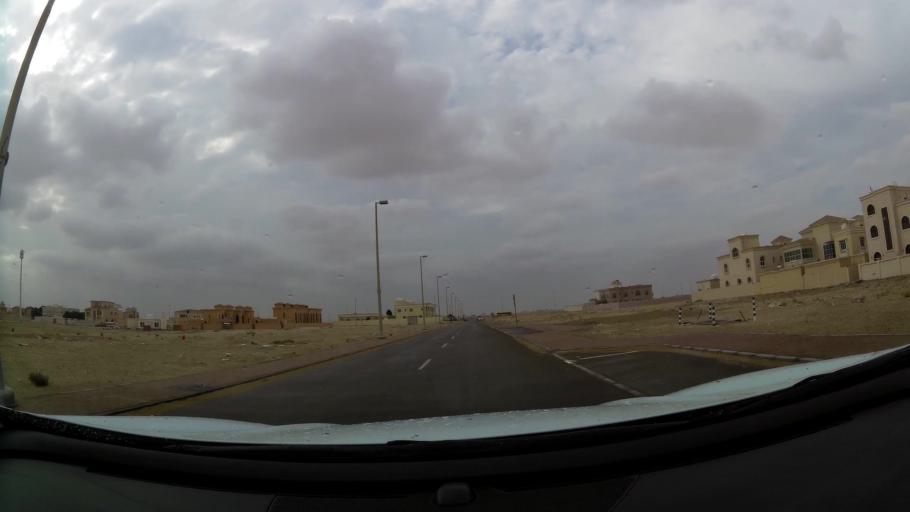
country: AE
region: Abu Dhabi
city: Abu Dhabi
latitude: 24.3595
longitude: 54.6194
